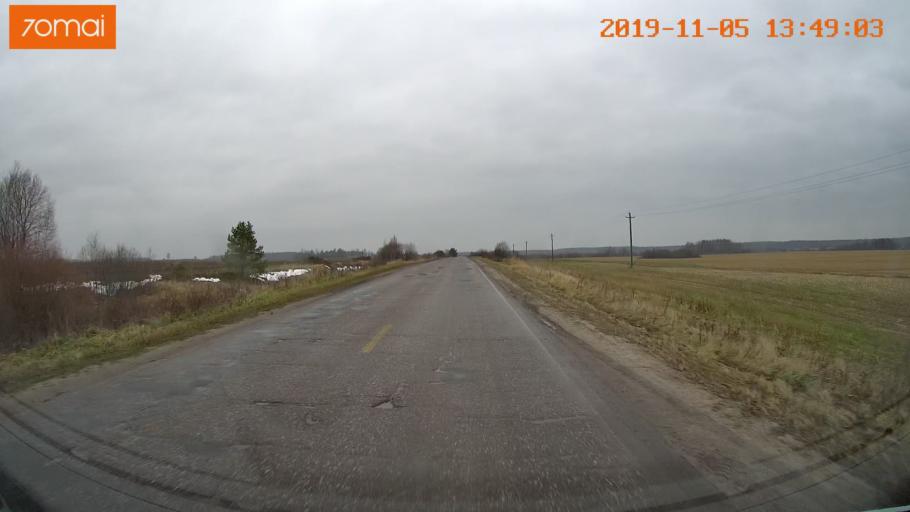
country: RU
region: Ivanovo
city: Kaminskiy
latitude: 57.0071
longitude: 41.4081
